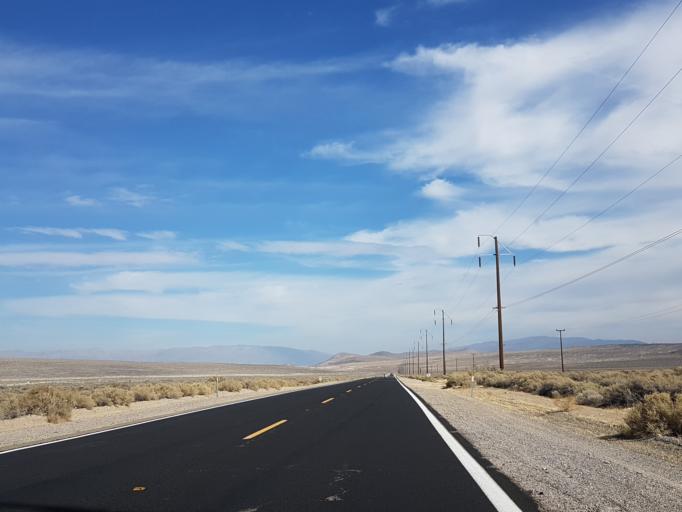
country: US
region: California
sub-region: San Bernardino County
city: Searles Valley
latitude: 35.6476
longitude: -117.5029
